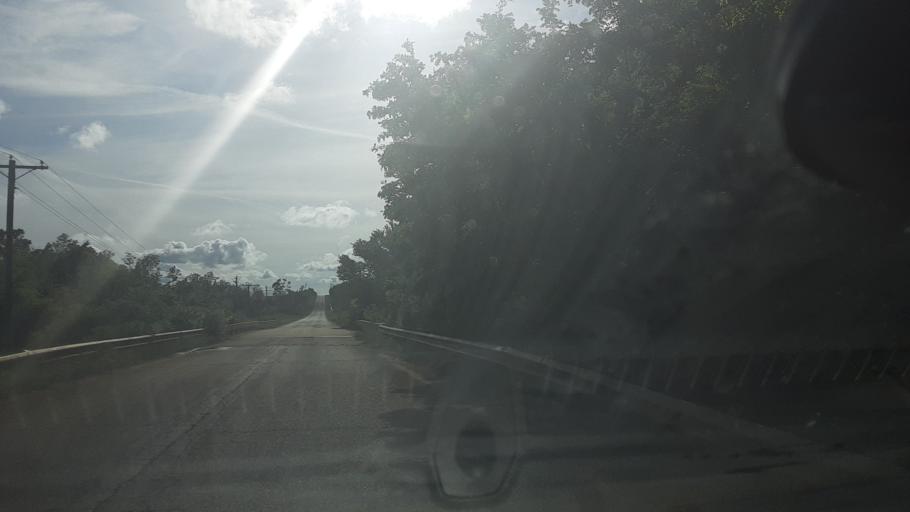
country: US
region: Oklahoma
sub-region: Logan County
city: Langston
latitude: 36.0577
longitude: -97.3877
